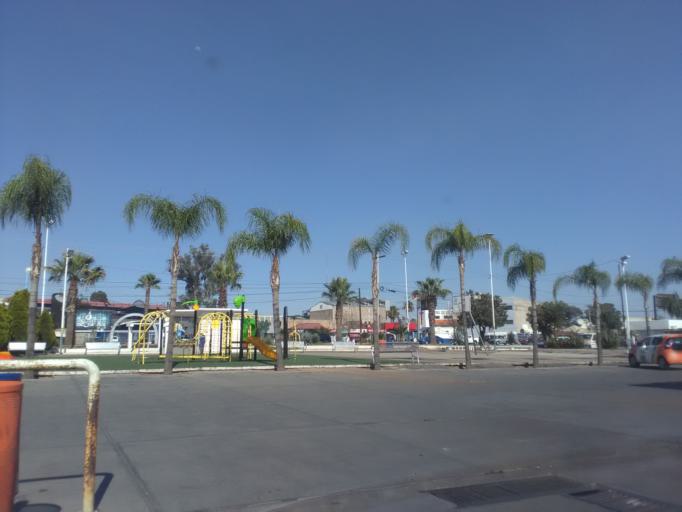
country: MX
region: Durango
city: Victoria de Durango
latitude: 24.0412
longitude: -104.6587
